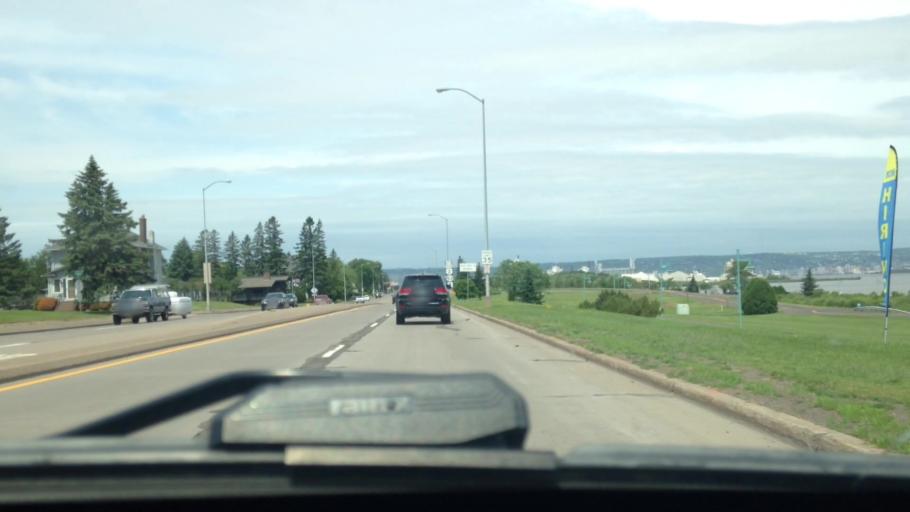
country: US
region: Wisconsin
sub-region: Douglas County
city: Superior
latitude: 46.7190
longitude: -92.0634
